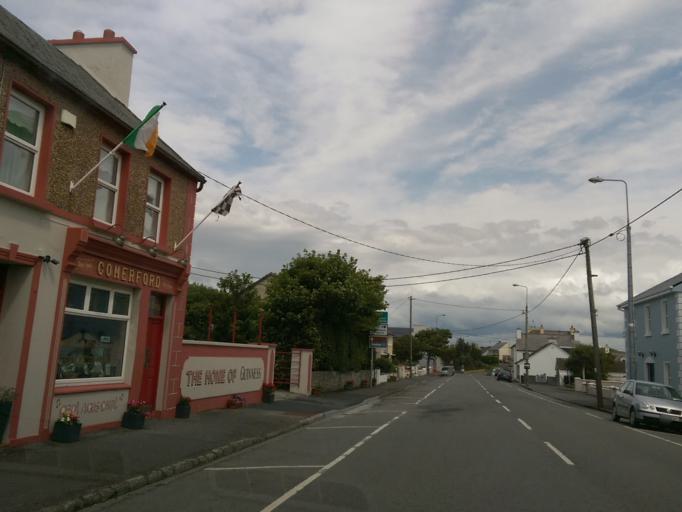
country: IE
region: Munster
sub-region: An Clar
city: Kilrush
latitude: 52.7308
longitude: -9.5264
